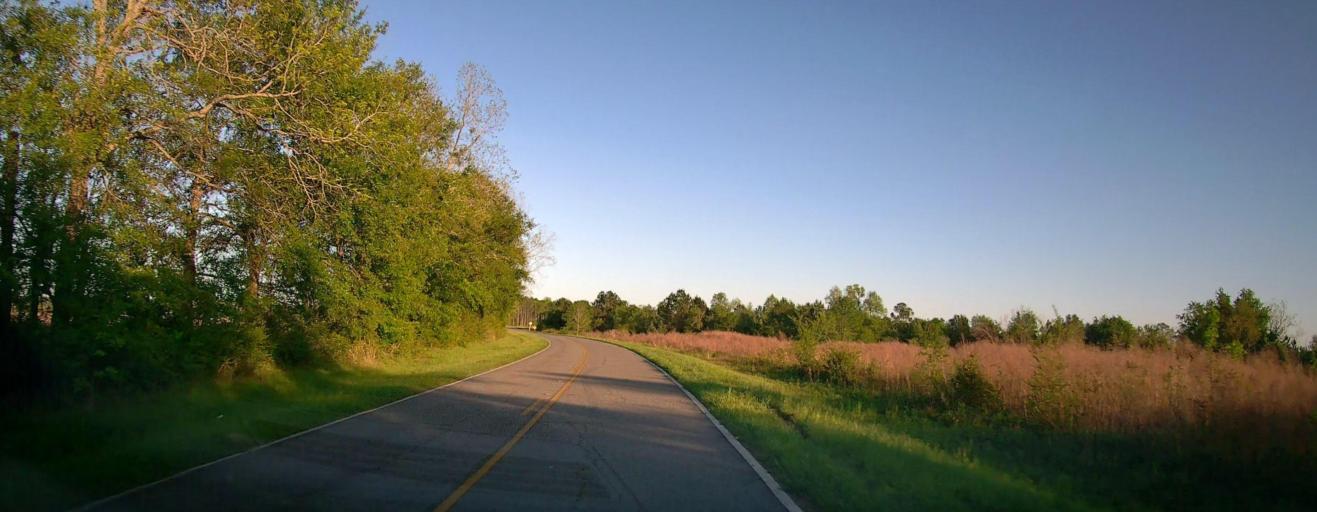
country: US
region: Georgia
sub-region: Ben Hill County
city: Fitzgerald
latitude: 31.6810
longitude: -83.2234
